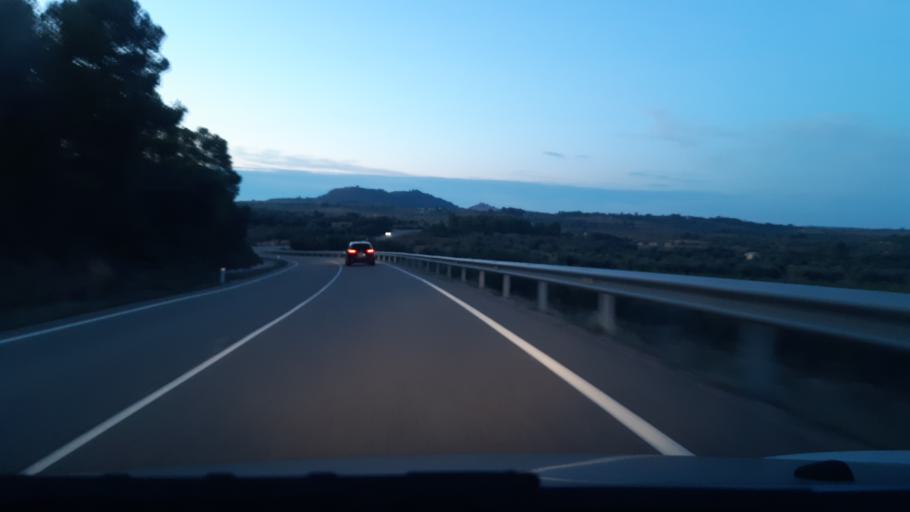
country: ES
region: Aragon
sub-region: Provincia de Teruel
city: Calaceite
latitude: 40.9821
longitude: 0.2016
